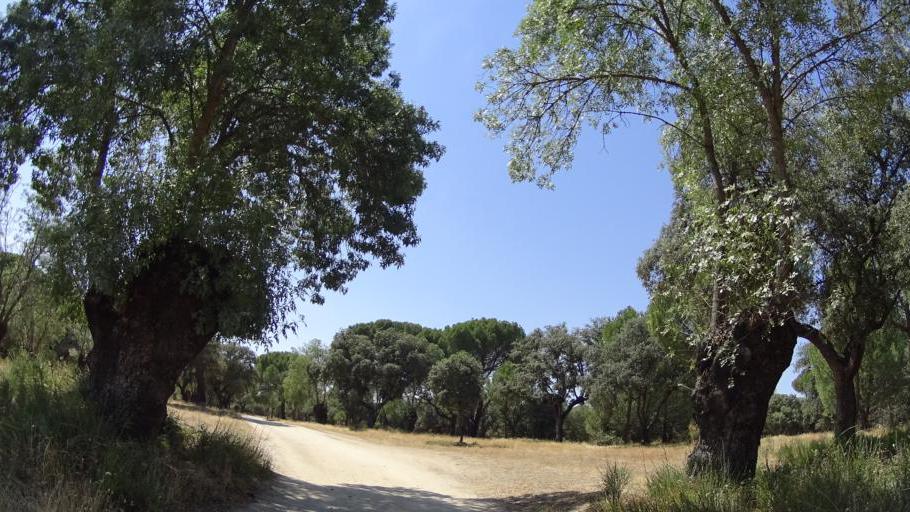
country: ES
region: Madrid
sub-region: Provincia de Madrid
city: Boadilla del Monte
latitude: 40.4226
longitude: -3.8550
